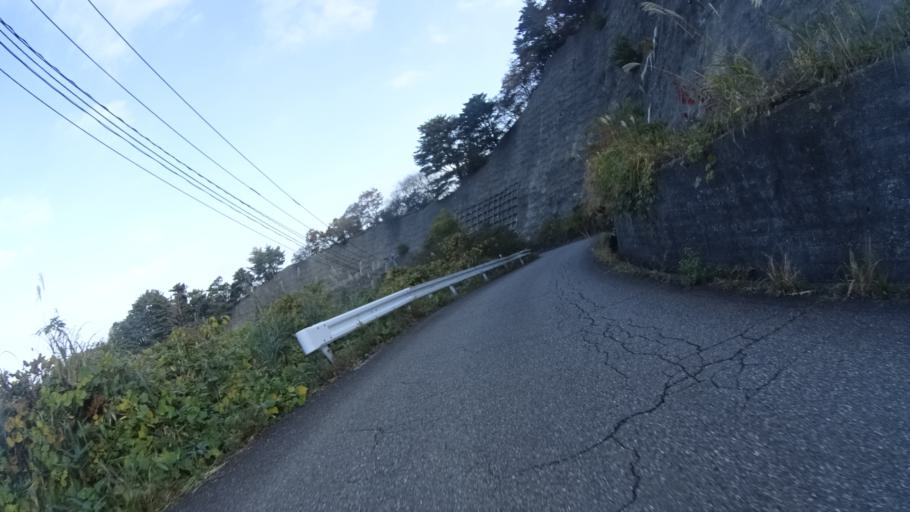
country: JP
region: Ishikawa
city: Nanao
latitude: 37.0133
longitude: 136.9864
